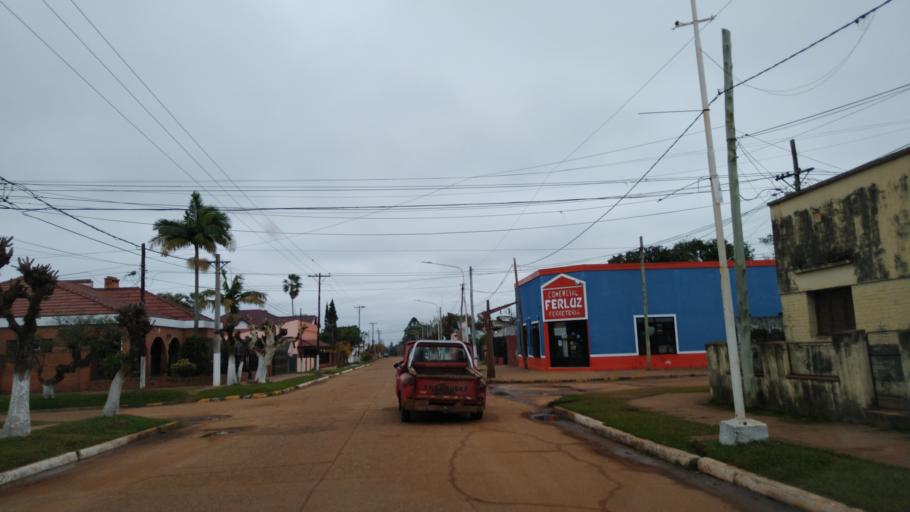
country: AR
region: Corrientes
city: Alvear
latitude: -29.0969
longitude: -56.5482
